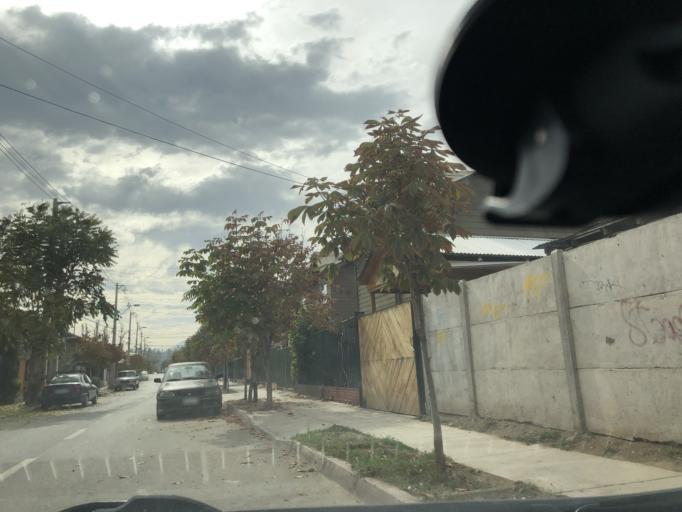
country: CL
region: Santiago Metropolitan
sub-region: Provincia de Cordillera
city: Puente Alto
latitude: -33.6132
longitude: -70.5273
